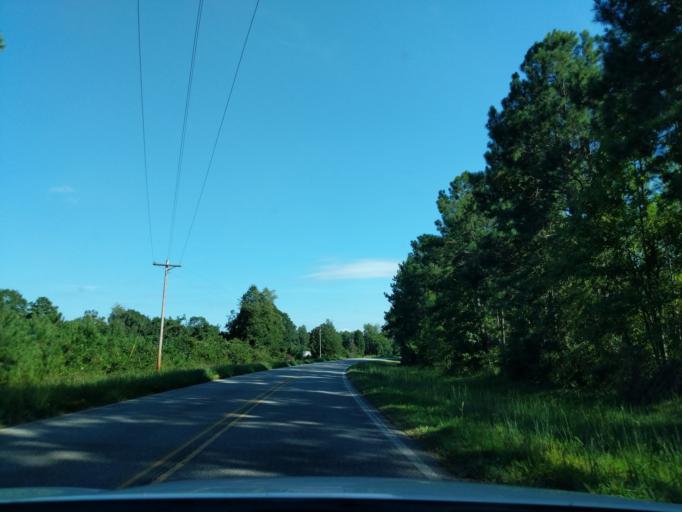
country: US
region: Georgia
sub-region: Oglethorpe County
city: Lexington
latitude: 33.9010
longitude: -82.9933
